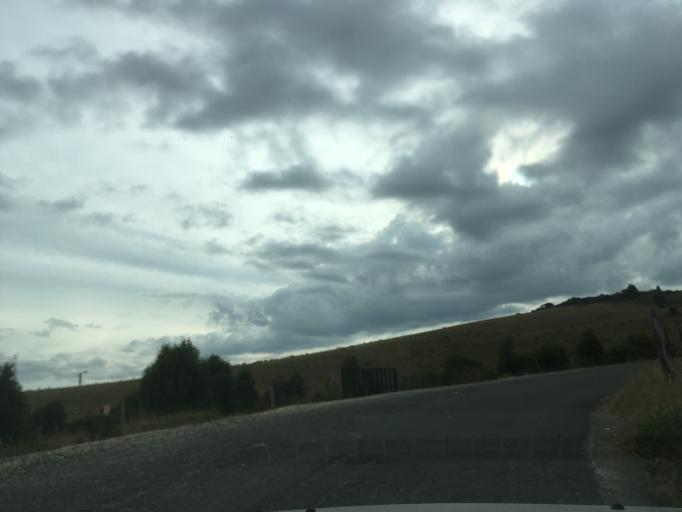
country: CO
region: Boyaca
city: Firavitoba
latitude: 5.6798
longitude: -73.0333
